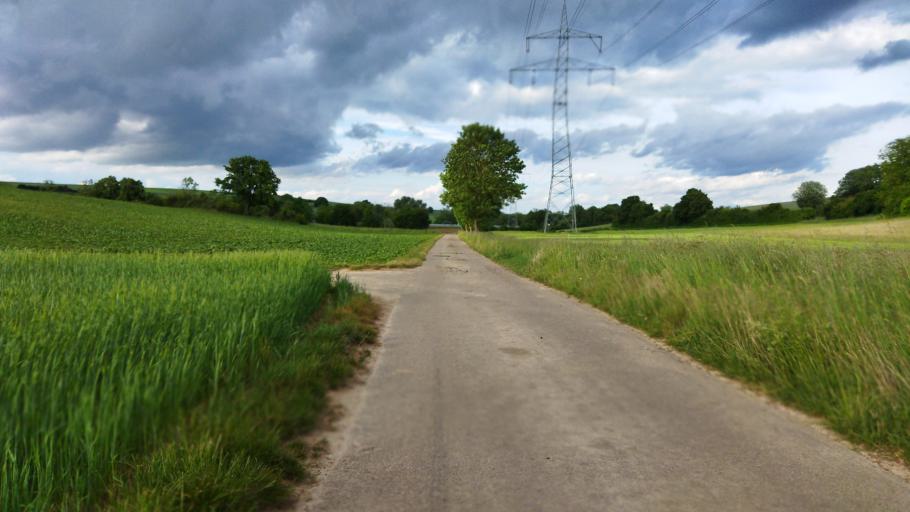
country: DE
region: Baden-Wuerttemberg
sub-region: Regierungsbezirk Stuttgart
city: Bad Wimpfen
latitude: 49.1858
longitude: 9.1535
